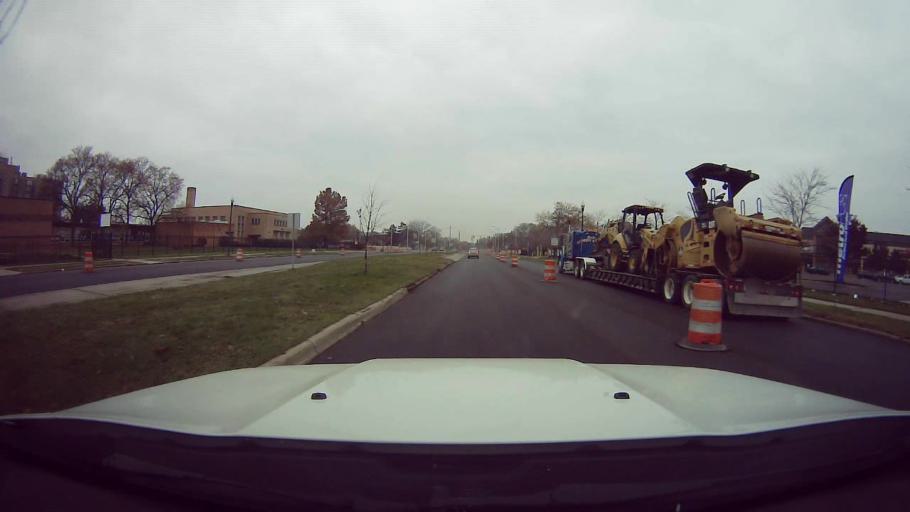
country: US
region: Michigan
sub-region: Oakland County
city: Oak Park
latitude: 42.4193
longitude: -83.2168
